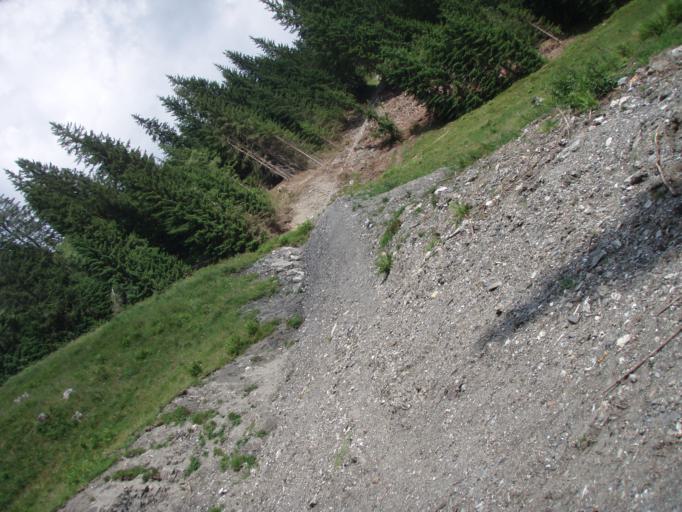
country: AT
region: Salzburg
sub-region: Politischer Bezirk Sankt Johann im Pongau
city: Dorfgastein
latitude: 47.2256
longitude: 13.0881
